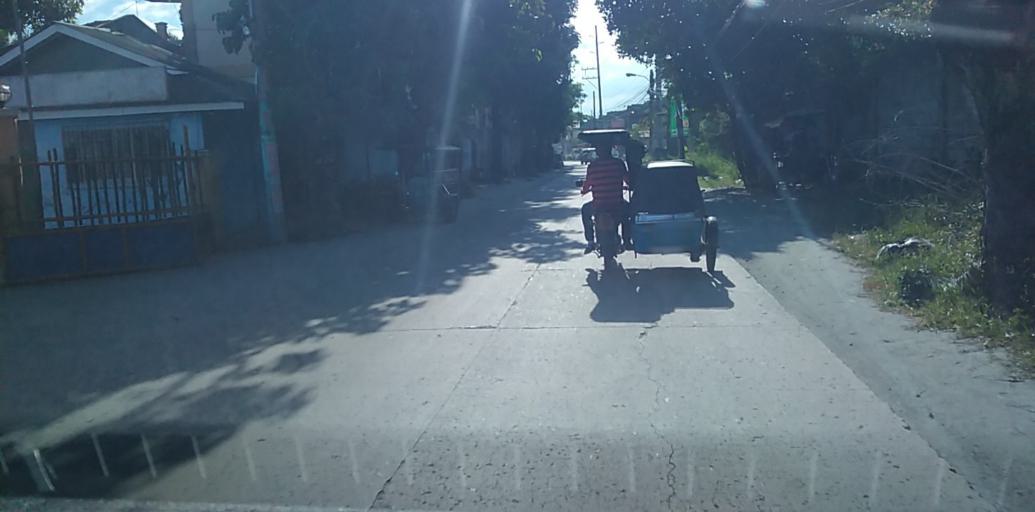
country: PH
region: Central Luzon
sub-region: Province of Pampanga
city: Acli
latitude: 15.1110
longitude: 120.6300
